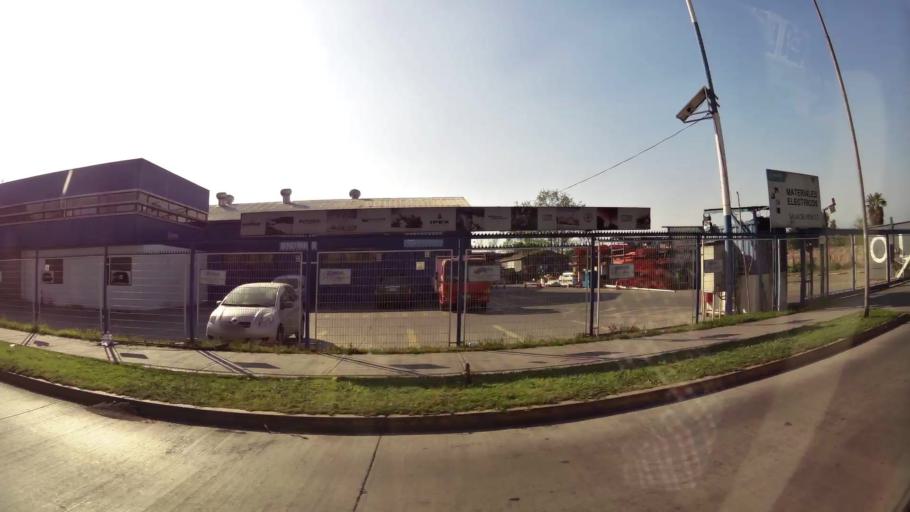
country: CL
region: Santiago Metropolitan
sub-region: Provincia de Santiago
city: Lo Prado
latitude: -33.4021
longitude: -70.6790
